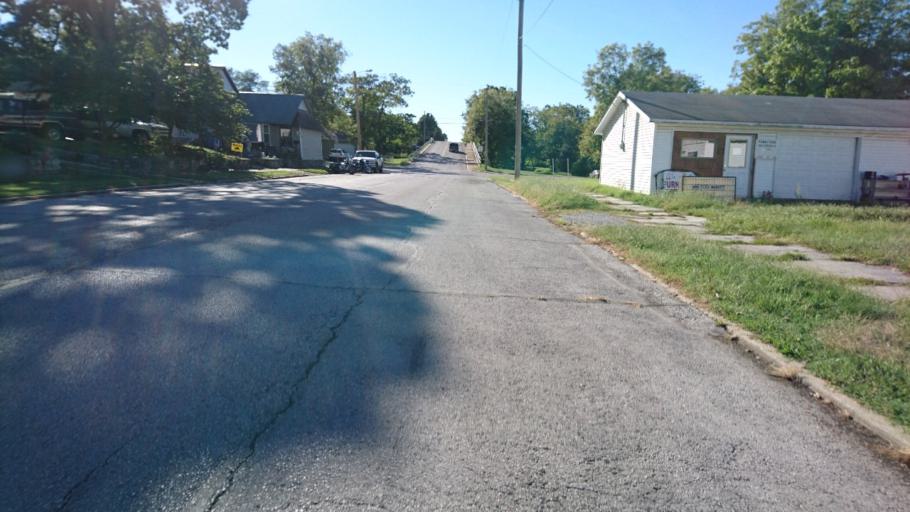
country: US
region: Missouri
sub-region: Jasper County
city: Carthage
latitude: 37.1764
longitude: -94.3167
